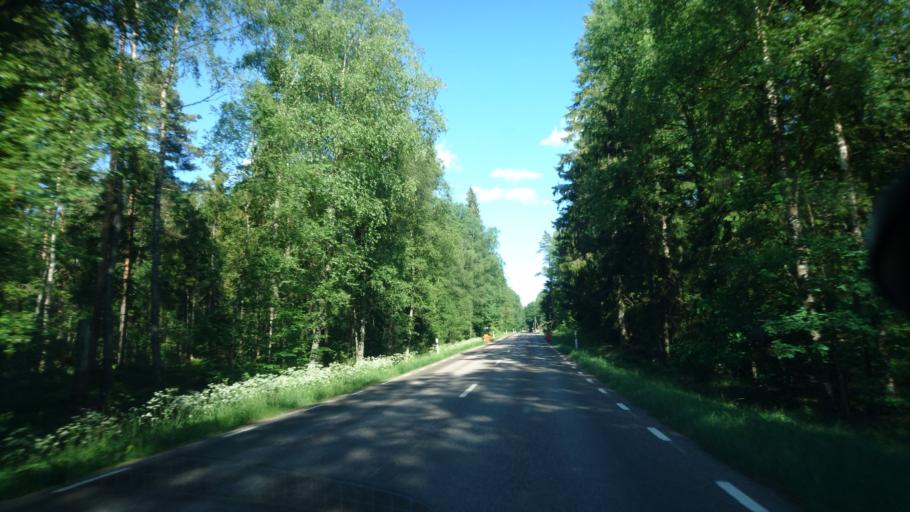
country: SE
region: Skane
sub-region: Osby Kommun
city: Lonsboda
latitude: 56.3911
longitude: 14.3509
